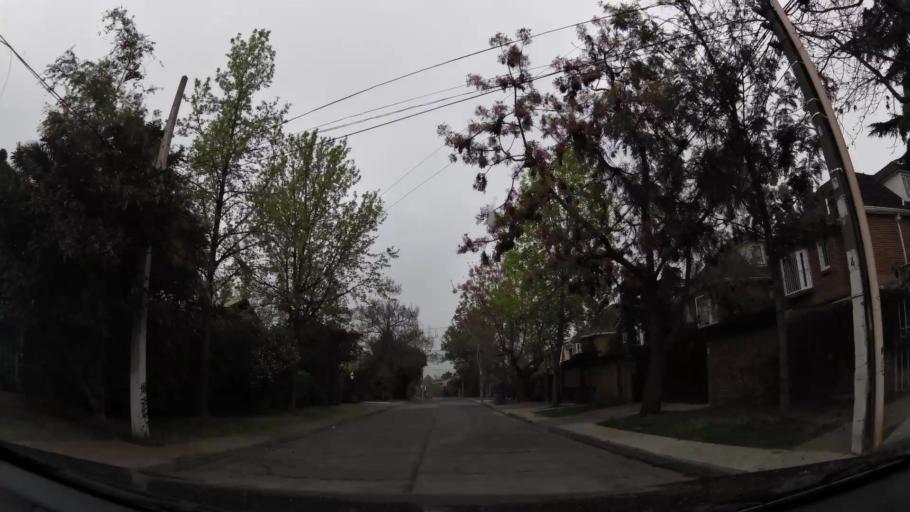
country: CL
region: Santiago Metropolitan
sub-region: Provincia de Santiago
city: Villa Presidente Frei, Nunoa, Santiago, Chile
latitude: -33.3846
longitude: -70.5410
